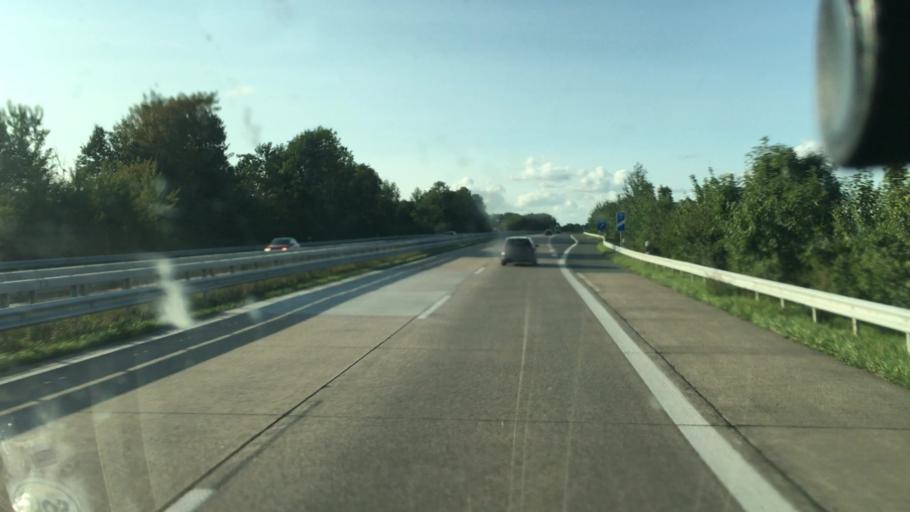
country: DE
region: Lower Saxony
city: Bockhorn
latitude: 53.4420
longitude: 8.0313
